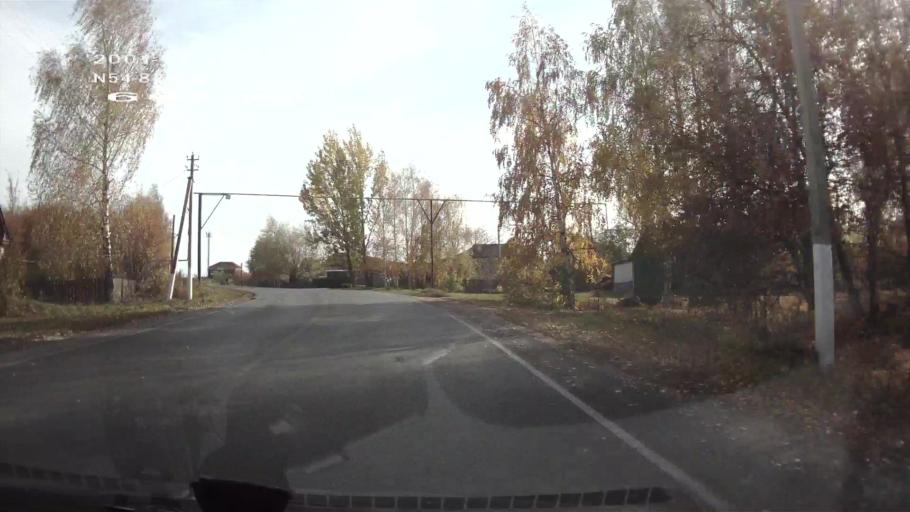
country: RU
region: Mordoviya
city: Turgenevo
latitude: 54.8444
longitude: 46.3490
